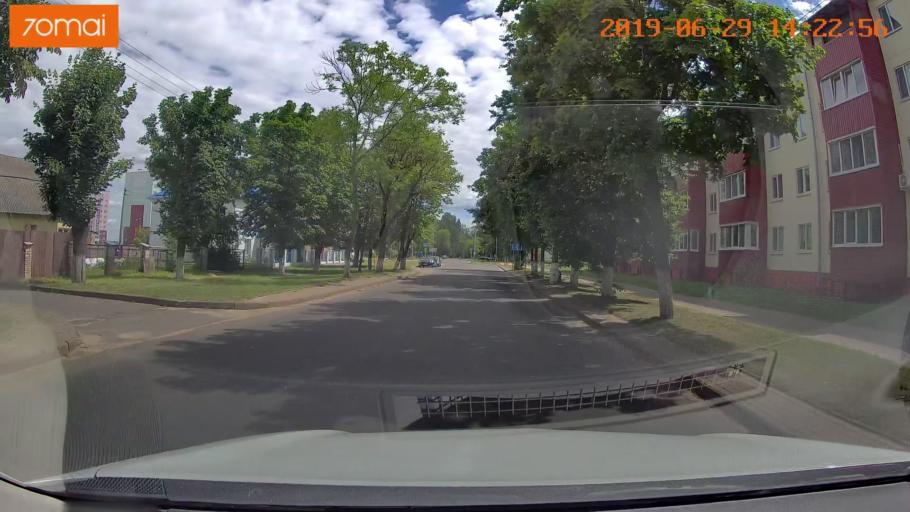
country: BY
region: Minsk
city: Salihorsk
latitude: 52.7888
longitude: 27.5524
